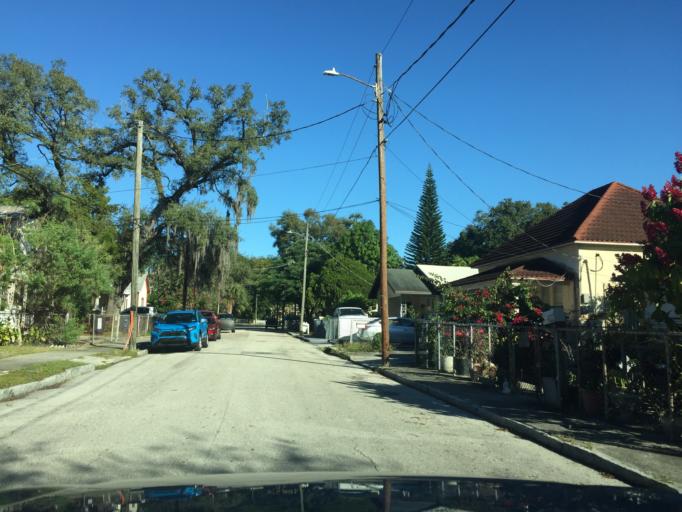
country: US
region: Florida
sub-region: Hillsborough County
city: Tampa
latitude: 27.9694
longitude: -82.4487
